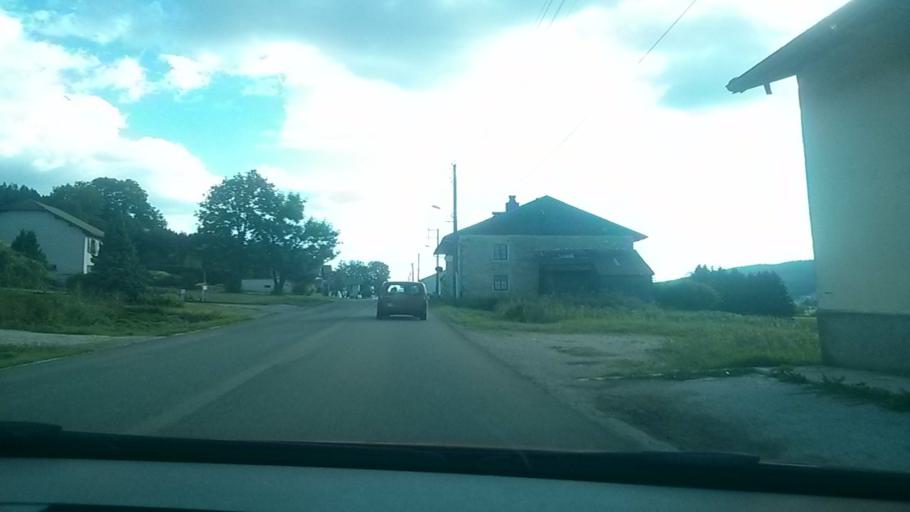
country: FR
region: Franche-Comte
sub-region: Departement du Jura
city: Les Rousses
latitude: 46.5255
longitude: 6.1287
